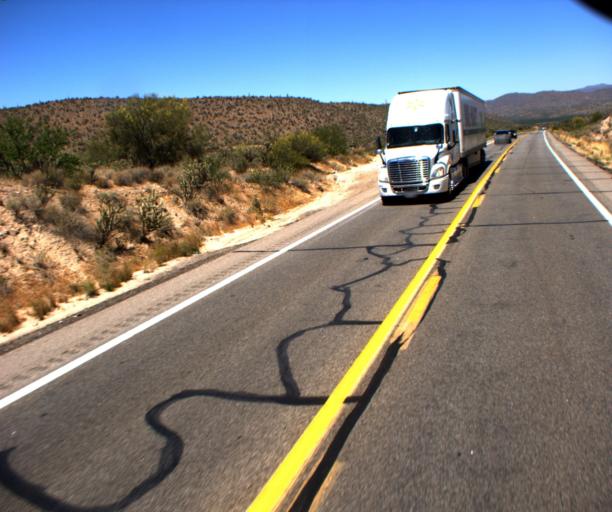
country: US
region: Arizona
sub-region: Yavapai County
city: Bagdad
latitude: 34.3484
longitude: -113.1622
